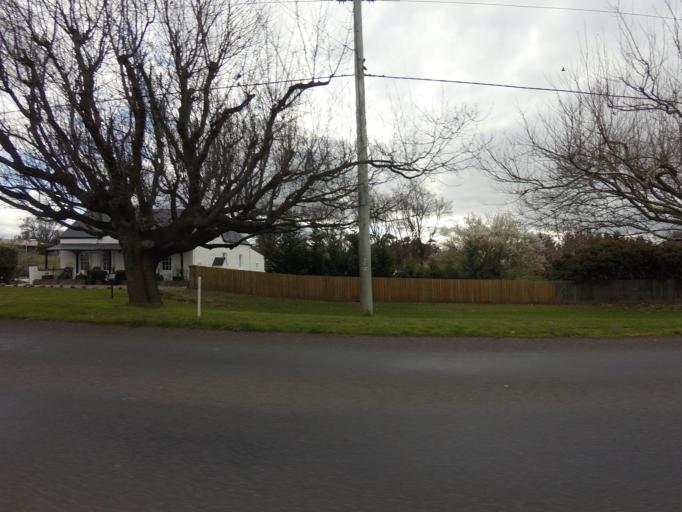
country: AU
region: Tasmania
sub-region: Northern Midlands
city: Evandale
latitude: -41.9363
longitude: 147.4920
